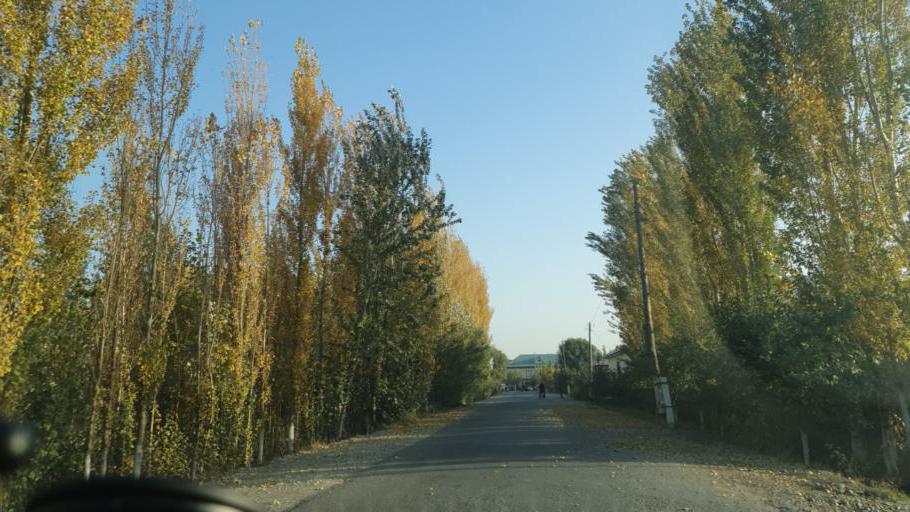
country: UZ
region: Fergana
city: Beshariq
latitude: 40.4636
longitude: 70.5432
